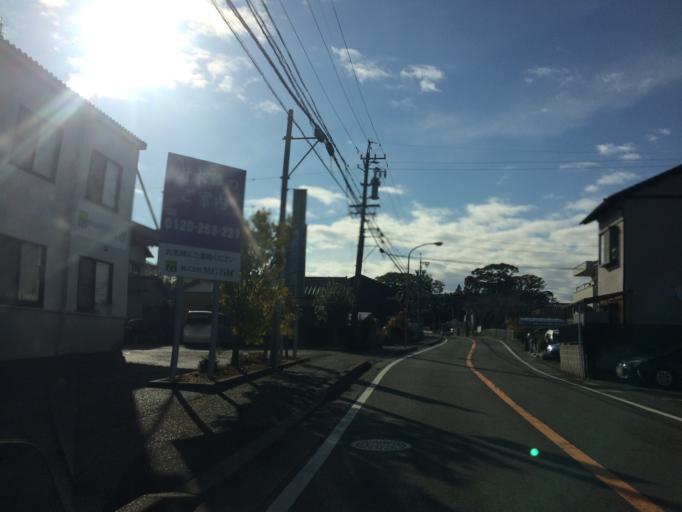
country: JP
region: Shizuoka
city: Shizuoka-shi
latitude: 34.9839
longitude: 138.4275
